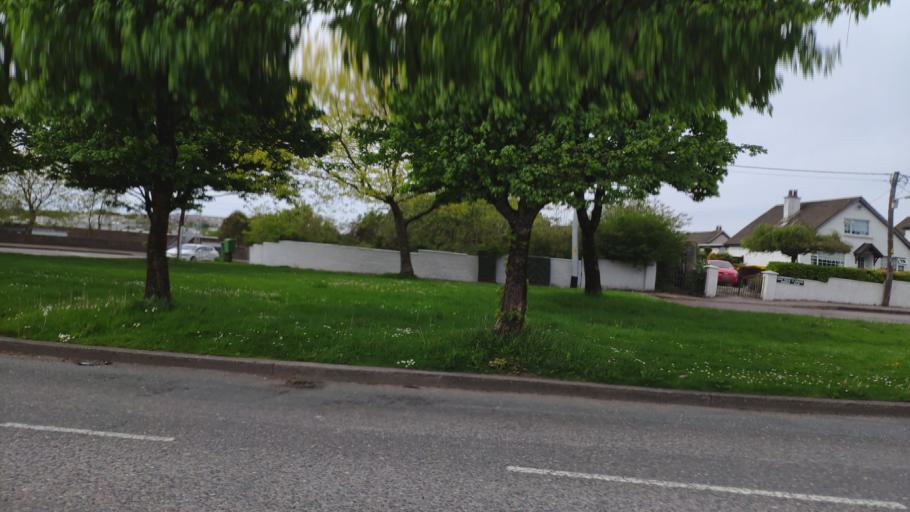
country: IE
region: Munster
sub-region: County Cork
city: Cork
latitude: 51.9174
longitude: -8.4469
